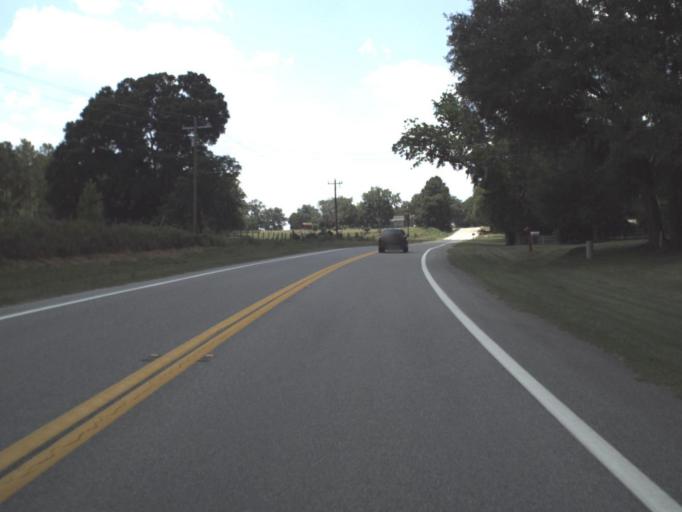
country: US
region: Florida
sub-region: Madison County
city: Madison
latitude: 30.5284
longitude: -83.6315
